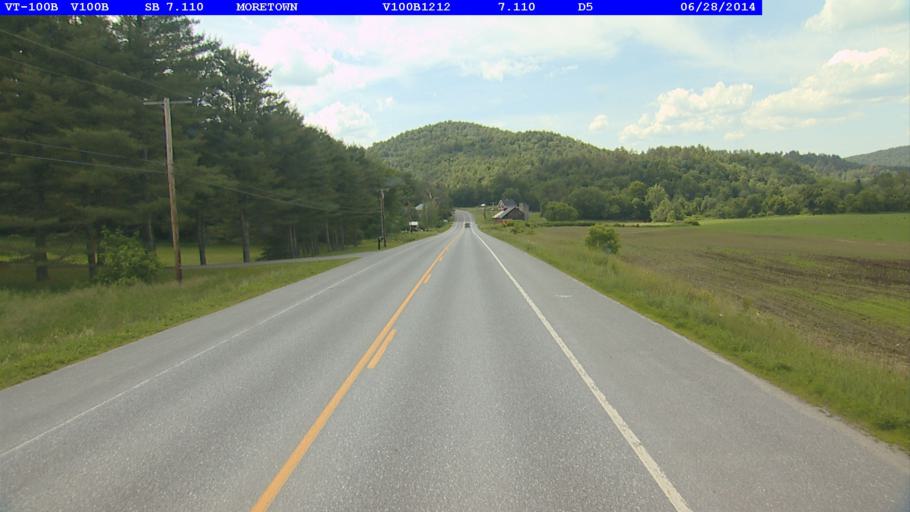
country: US
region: Vermont
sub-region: Washington County
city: Waterbury
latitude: 44.2945
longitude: -72.6925
